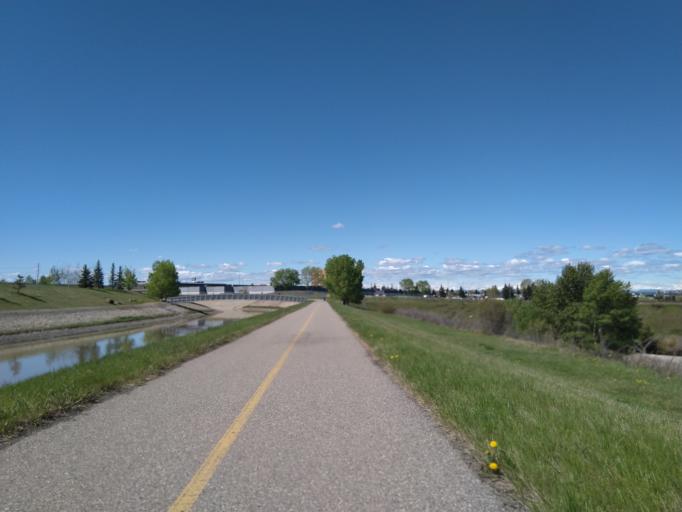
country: CA
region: Alberta
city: Calgary
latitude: 50.9831
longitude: -113.9917
